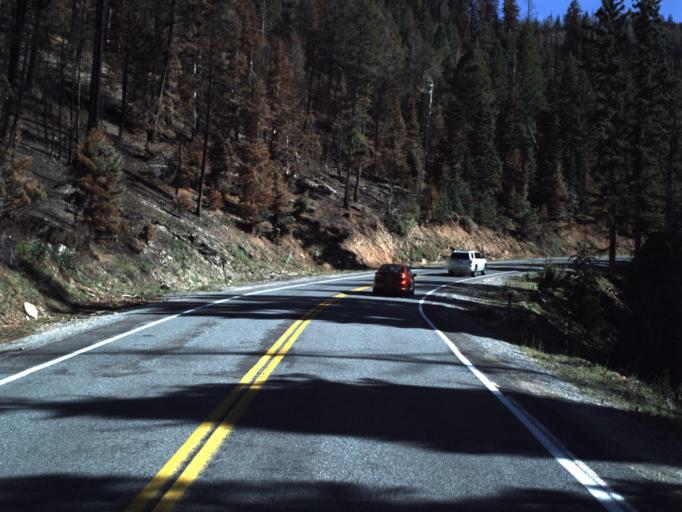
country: US
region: Utah
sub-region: Iron County
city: Parowan
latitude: 37.7346
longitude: -112.8373
